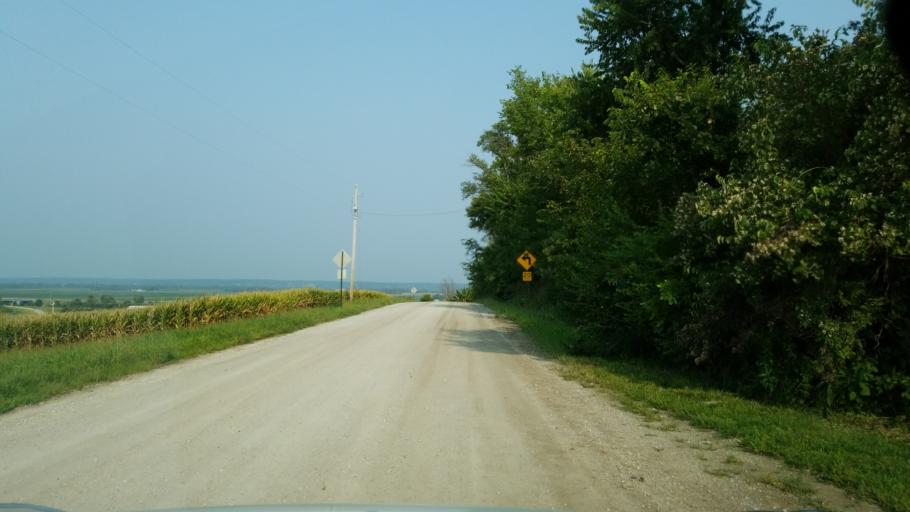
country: US
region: Nebraska
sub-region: Sarpy County
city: Offutt Air Force Base
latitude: 41.0748
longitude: -95.9318
